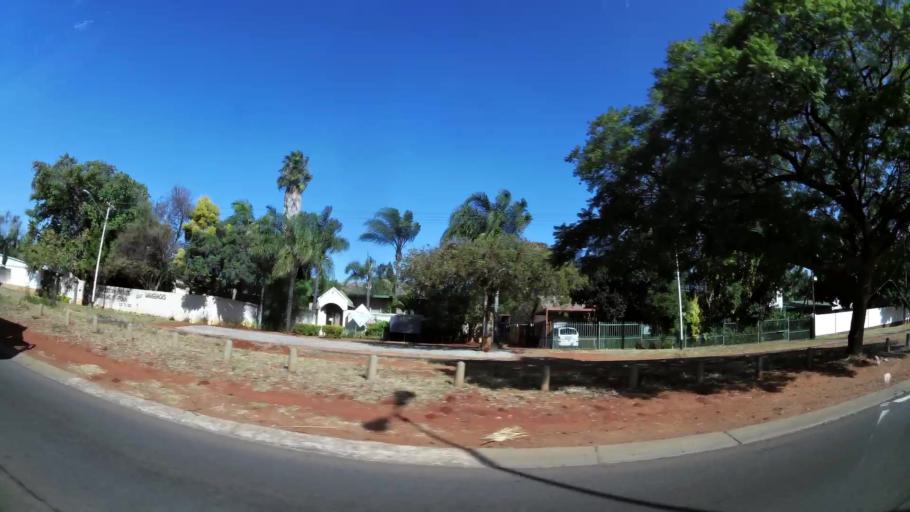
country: ZA
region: Gauteng
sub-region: City of Tshwane Metropolitan Municipality
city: Pretoria
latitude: -25.6811
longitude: 28.2201
